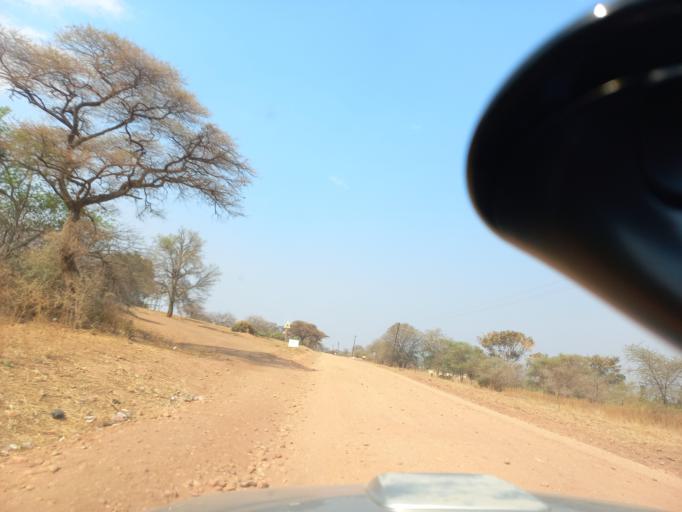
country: ZW
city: Chirundu
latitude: -15.9300
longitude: 28.9650
